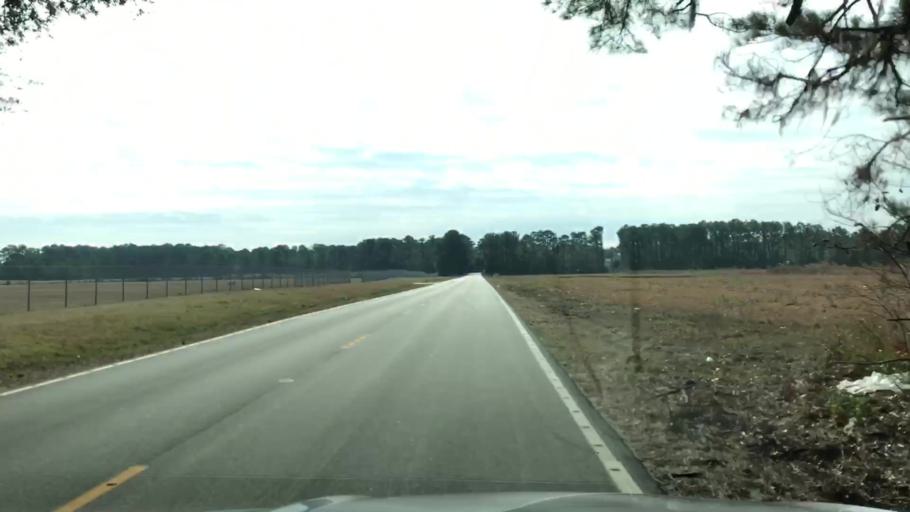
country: US
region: South Carolina
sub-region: Charleston County
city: Folly Beach
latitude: 32.7064
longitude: -80.0166
